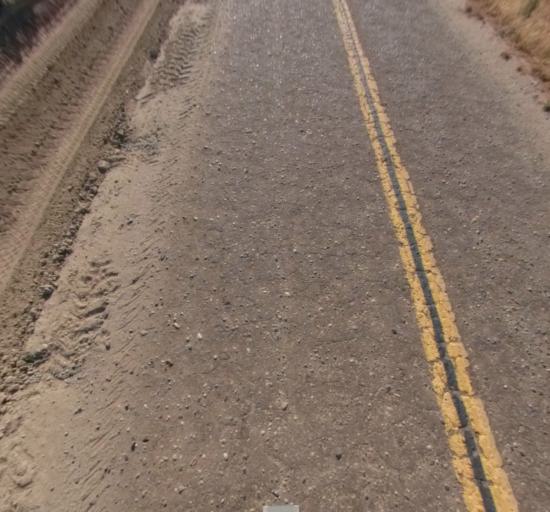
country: US
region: California
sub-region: Fresno County
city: Biola
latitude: 36.8440
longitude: -120.0933
